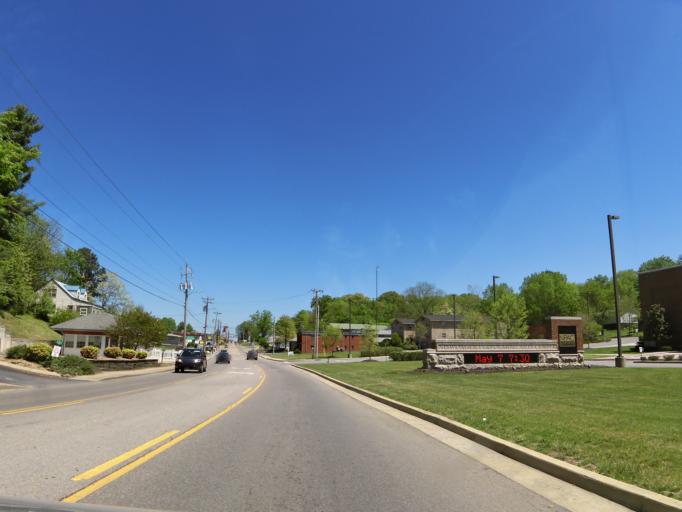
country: US
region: Tennessee
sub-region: Greene County
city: Greeneville
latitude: 36.1666
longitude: -82.8250
